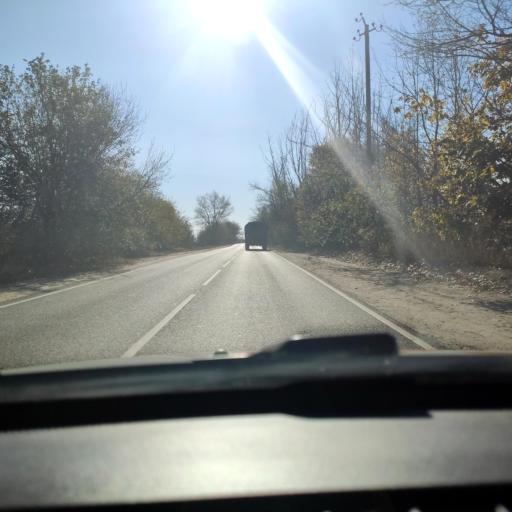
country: RU
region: Voronezj
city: Shilovo
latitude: 51.5684
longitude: 39.1391
